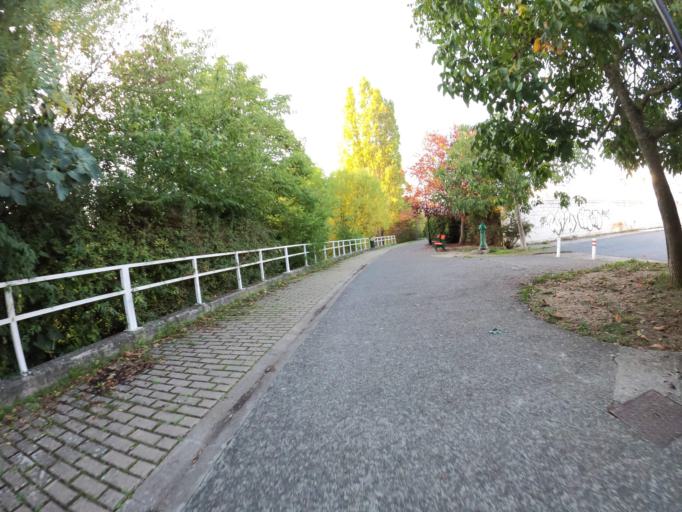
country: ES
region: Navarre
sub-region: Provincia de Navarra
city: Baranain
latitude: 42.8105
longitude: -1.6813
